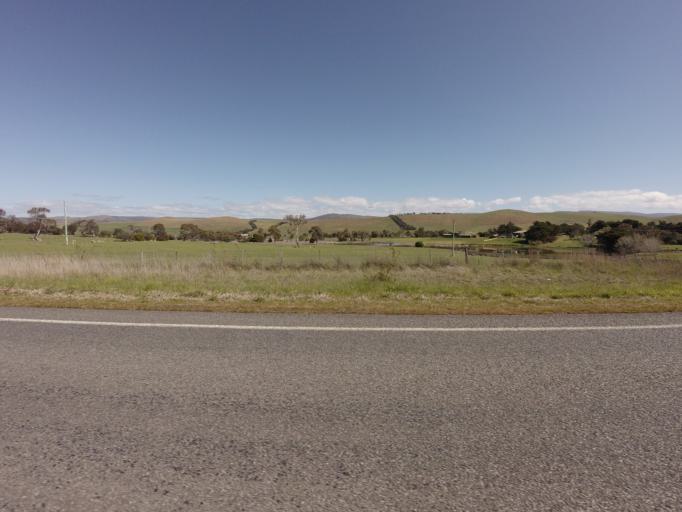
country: AU
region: Tasmania
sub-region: Derwent Valley
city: New Norfolk
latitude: -42.5504
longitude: 146.7910
